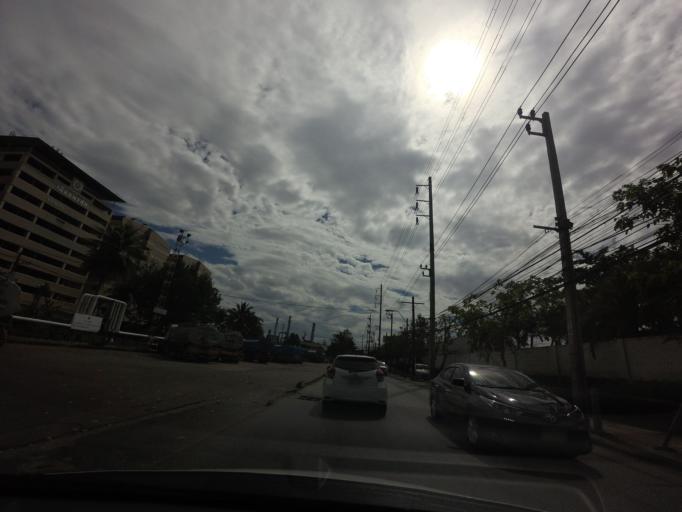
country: TH
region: Bangkok
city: Phra Khanong
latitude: 13.6918
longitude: 100.5903
